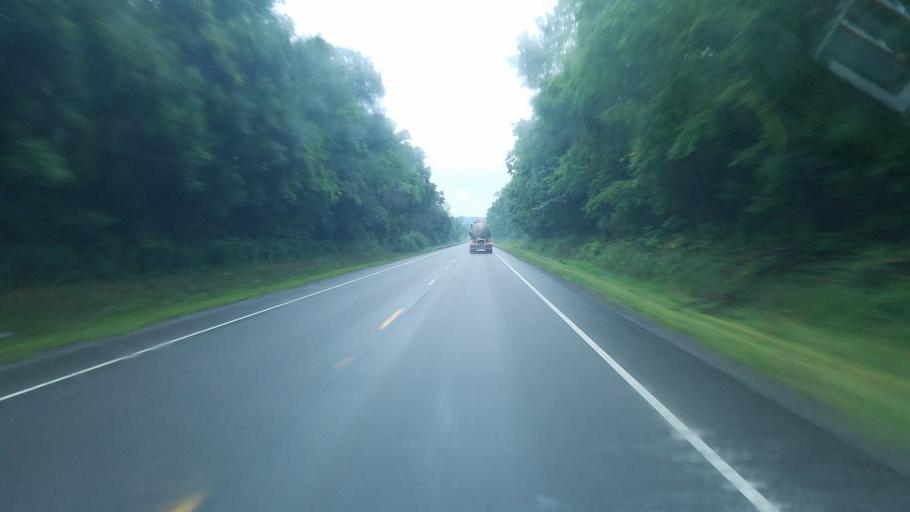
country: US
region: Ohio
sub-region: Coshocton County
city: Coshocton
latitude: 40.2876
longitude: -81.8822
